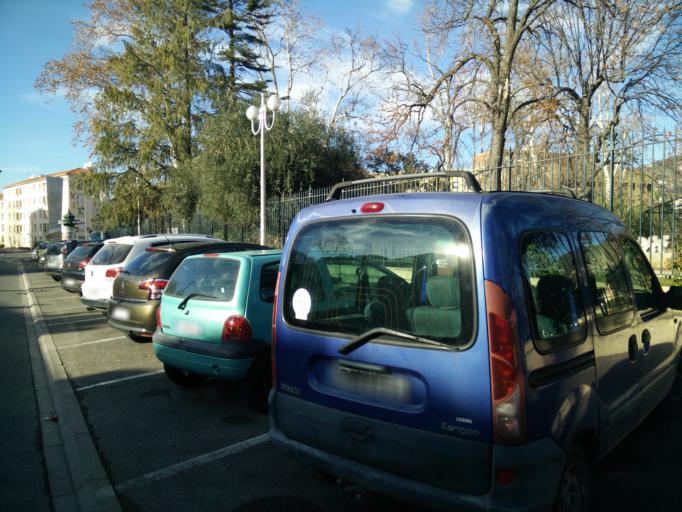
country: FR
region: Provence-Alpes-Cote d'Azur
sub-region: Departement du Var
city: Draguignan
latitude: 43.5379
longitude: 6.4595
